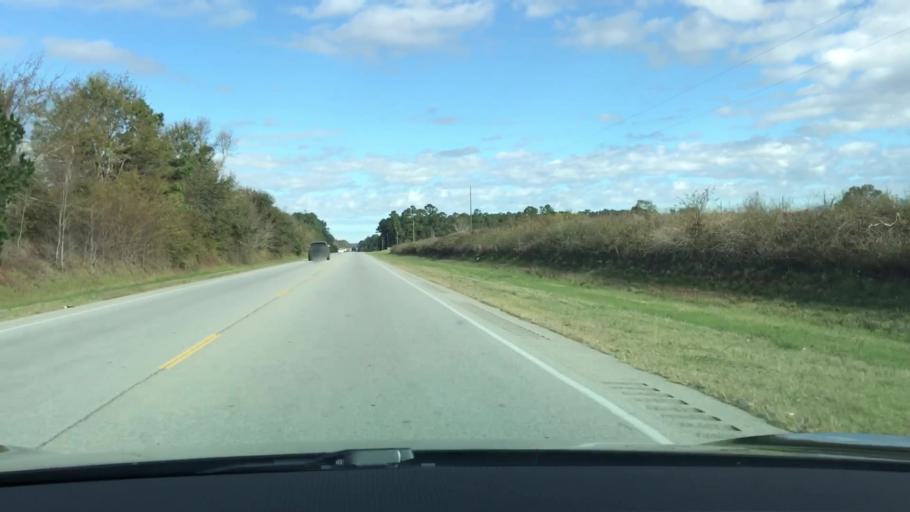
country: US
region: Georgia
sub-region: Jefferson County
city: Wadley
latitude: 32.9301
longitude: -82.3968
